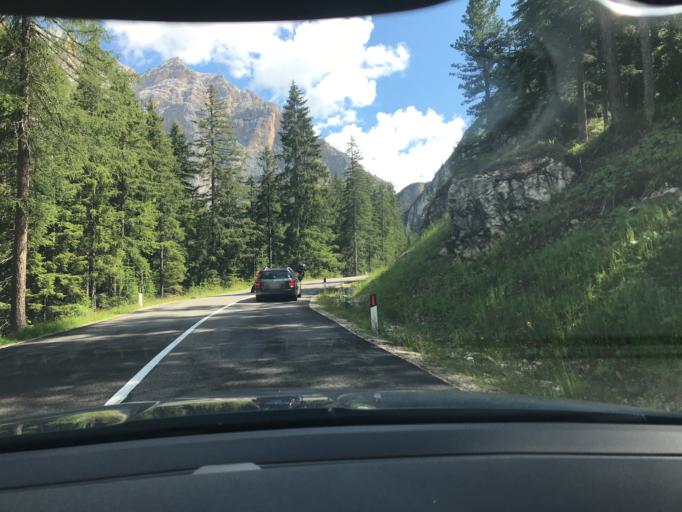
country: IT
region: Veneto
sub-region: Provincia di Belluno
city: Livinallongo del Col di Lana
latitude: 46.5511
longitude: 11.9738
